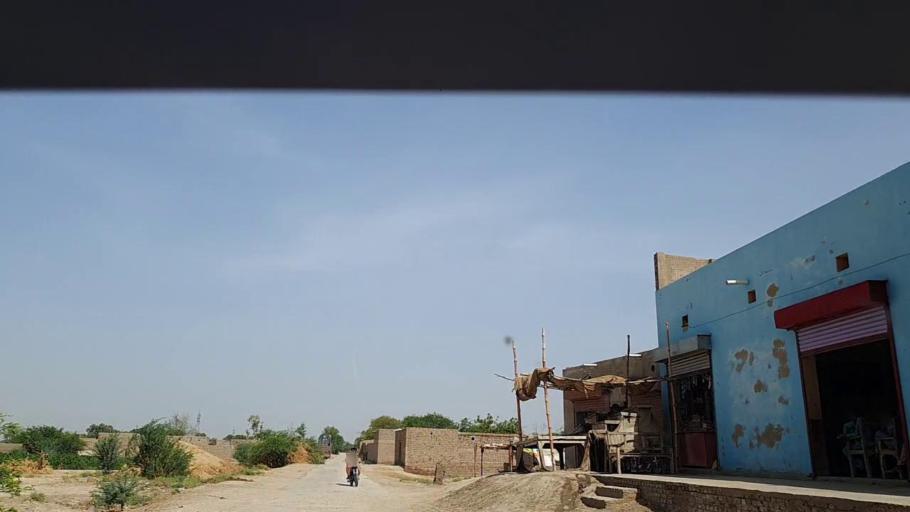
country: PK
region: Sindh
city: Phulji
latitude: 26.9625
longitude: 67.6926
